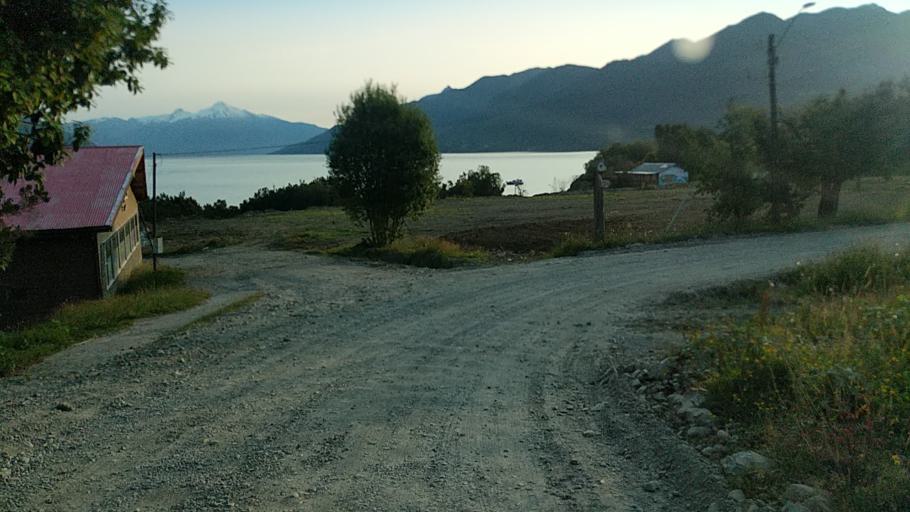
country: CL
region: Los Lagos
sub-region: Provincia de Llanquihue
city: La Ensenada
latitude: -41.4936
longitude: -72.3054
